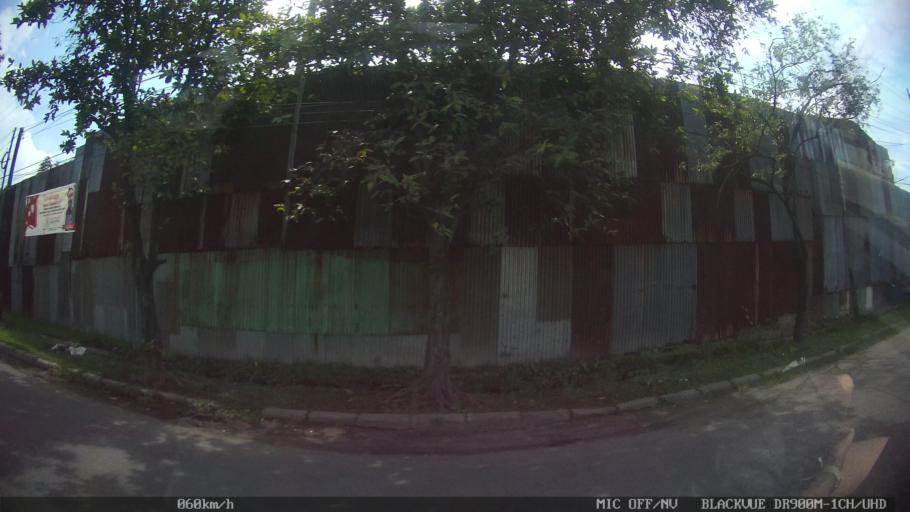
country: ID
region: North Sumatra
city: Labuhan Deli
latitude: 3.6690
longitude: 98.6672
